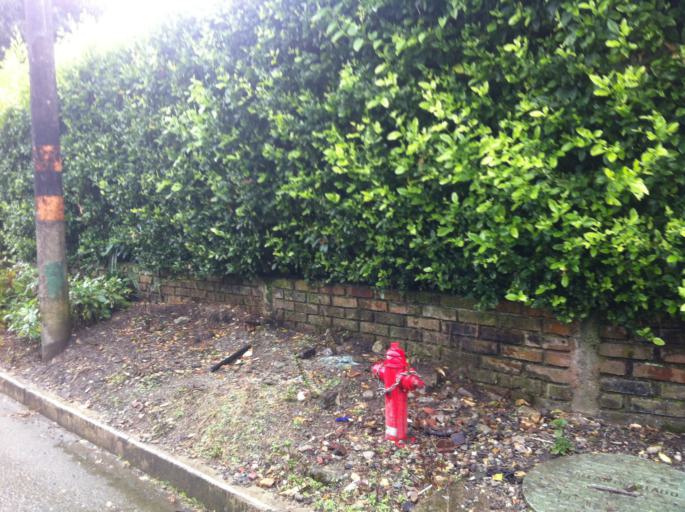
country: CO
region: Quindio
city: Genova
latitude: 4.2073
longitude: -75.7930
